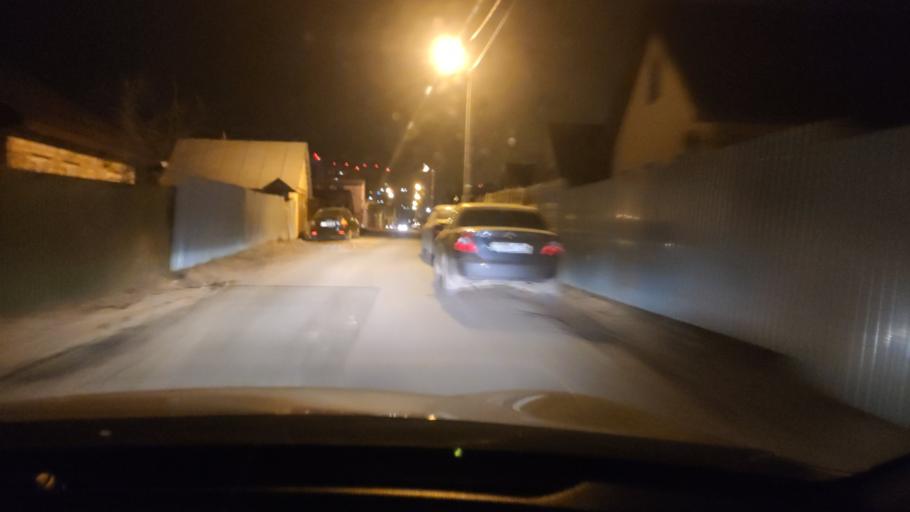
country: RU
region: Tatarstan
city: Osinovo
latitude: 55.8473
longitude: 48.8962
